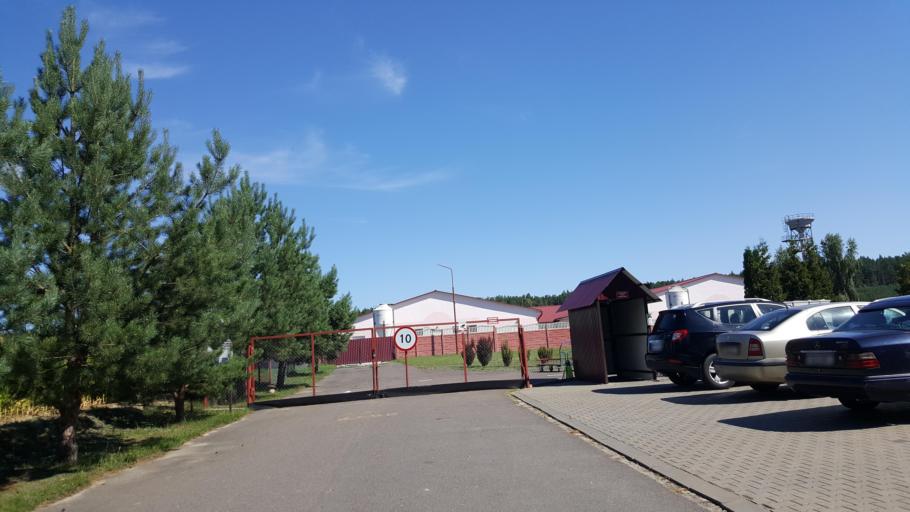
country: BY
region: Brest
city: Charnawchytsy
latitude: 52.2893
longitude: 23.7805
